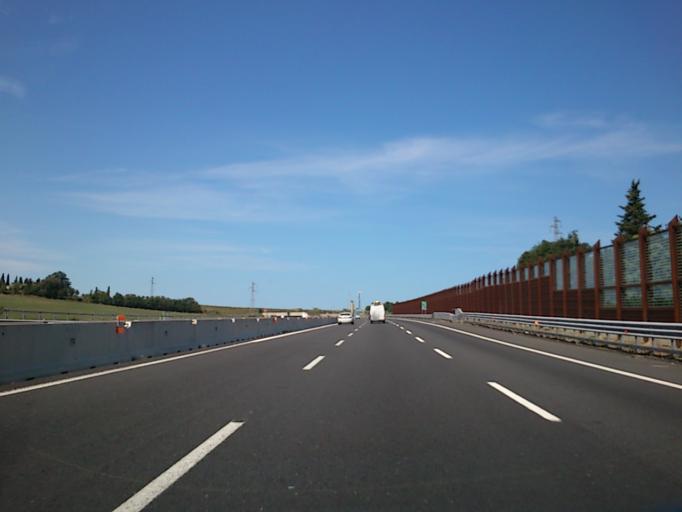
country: IT
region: The Marches
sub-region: Provincia di Pesaro e Urbino
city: Borgo Santa Maria
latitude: 43.9176
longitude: 12.8155
